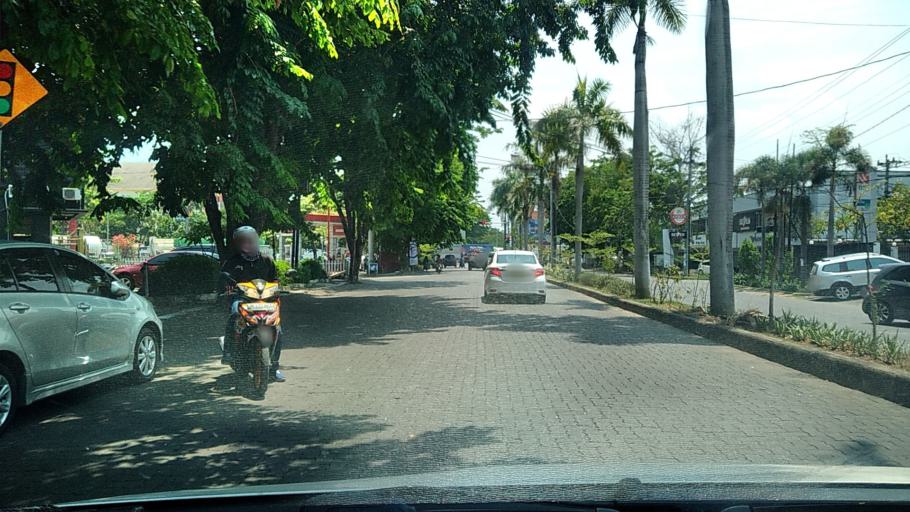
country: ID
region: Central Java
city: Semarang
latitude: -6.9694
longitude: 110.3906
